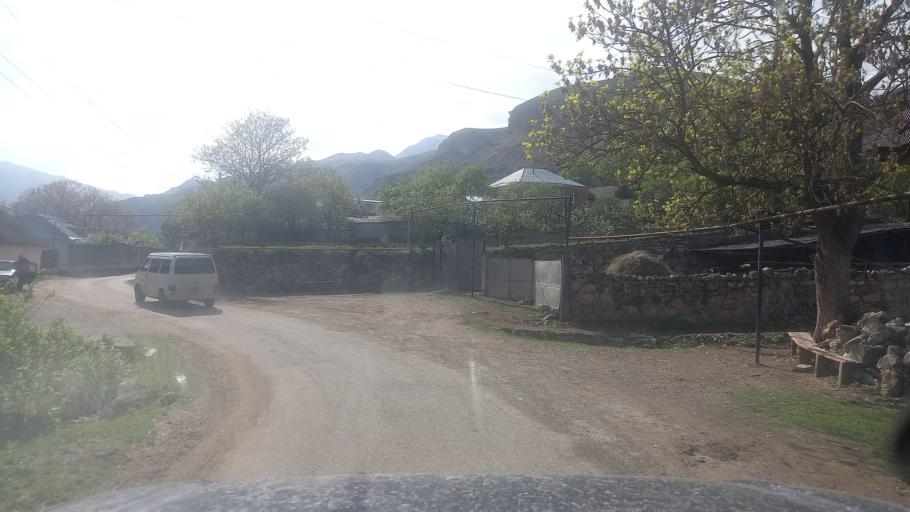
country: RU
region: Kabardino-Balkariya
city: Kamennomostskoye
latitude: 43.7256
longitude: 42.9156
